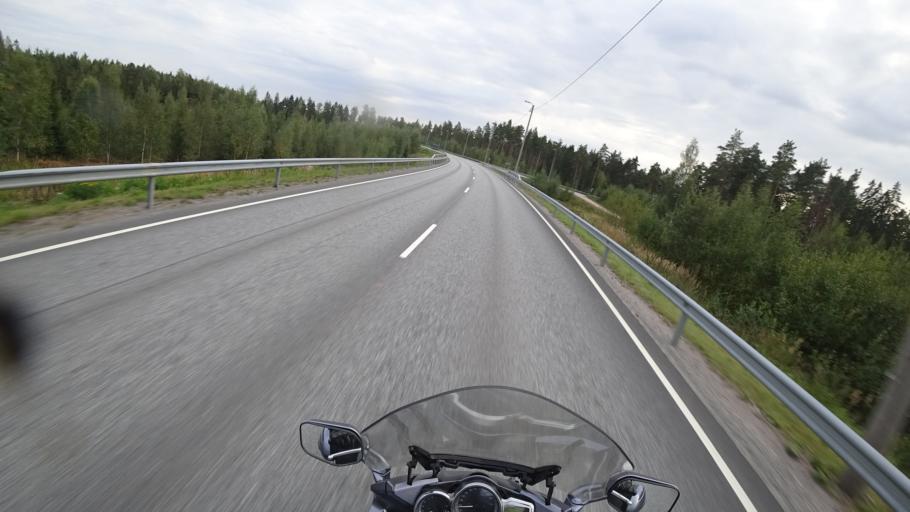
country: FI
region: Uusimaa
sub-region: Raaseporin
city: Karis
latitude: 60.0659
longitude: 23.6300
